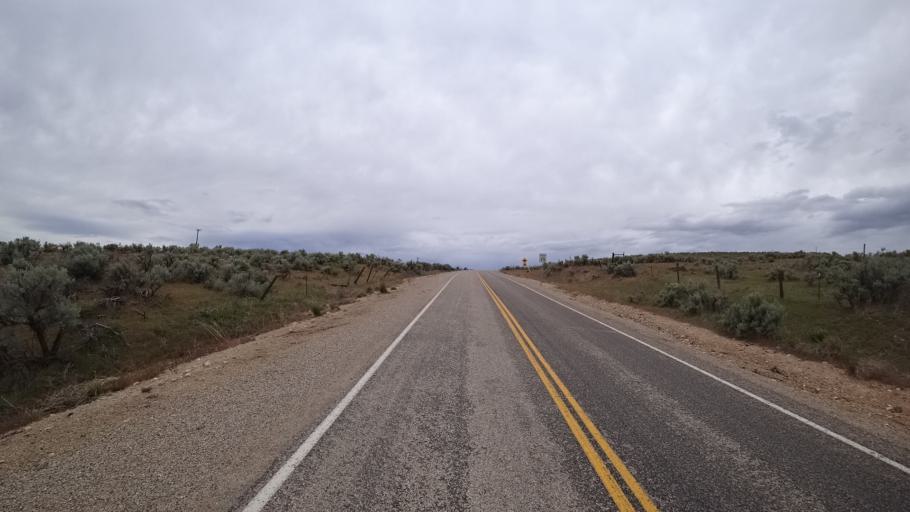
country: US
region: Idaho
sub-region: Ada County
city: Boise
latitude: 43.4780
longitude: -115.9926
